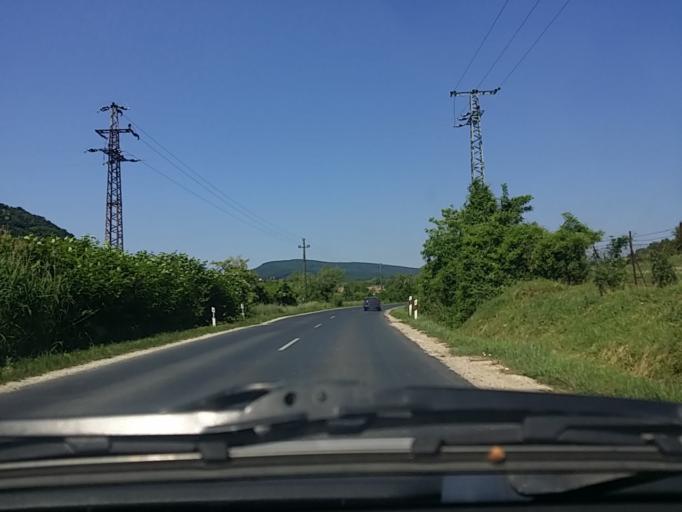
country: HU
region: Pest
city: Csobanka
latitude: 47.6531
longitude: 18.9857
